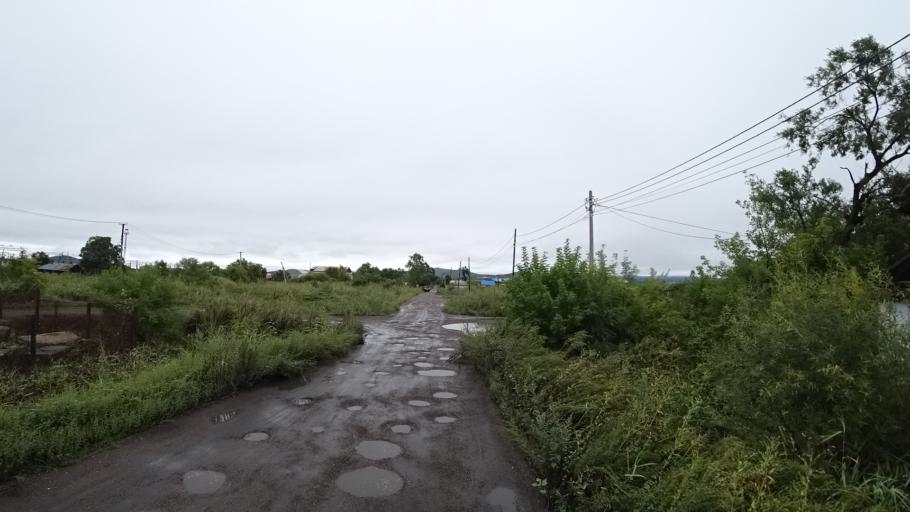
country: RU
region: Primorskiy
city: Monastyrishche
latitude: 44.2106
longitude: 132.4436
